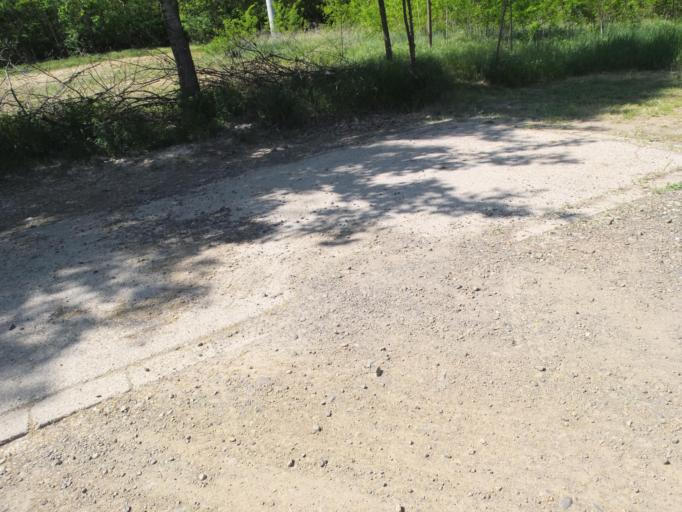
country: HU
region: Pest
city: Fot
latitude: 47.6513
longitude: 19.2308
